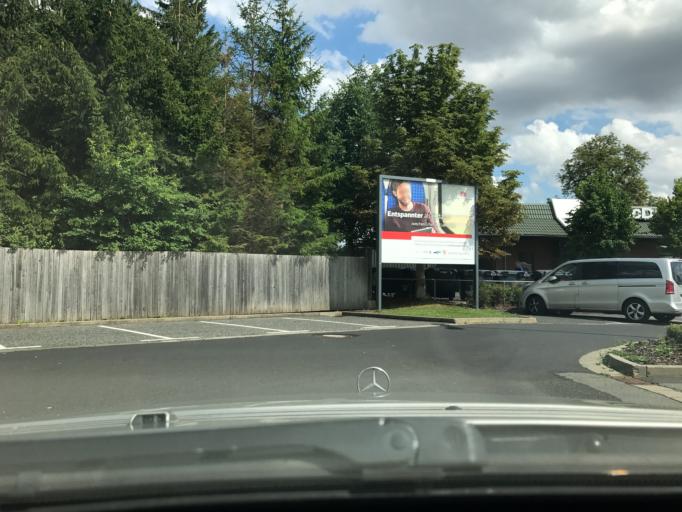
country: DE
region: Thuringia
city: Muehlhausen
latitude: 51.2234
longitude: 10.4524
